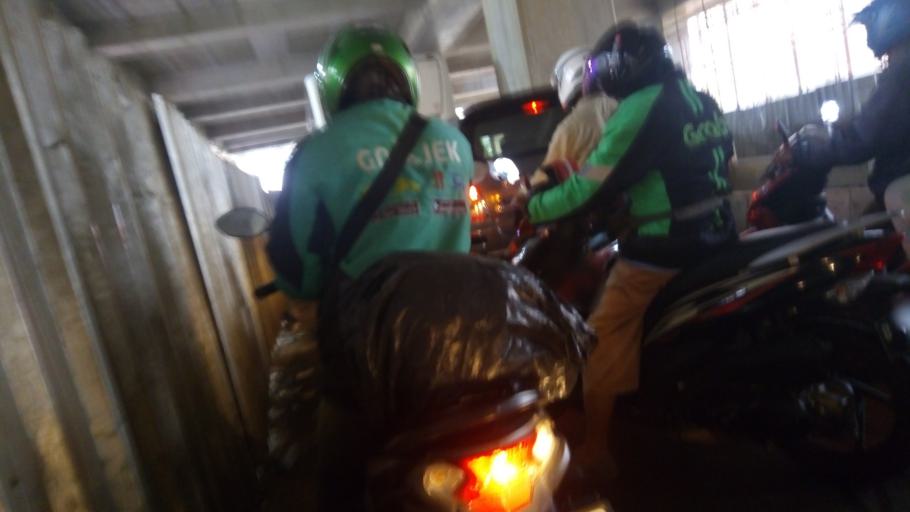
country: ID
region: Jakarta Raya
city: Jakarta
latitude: -6.2391
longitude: 106.7984
